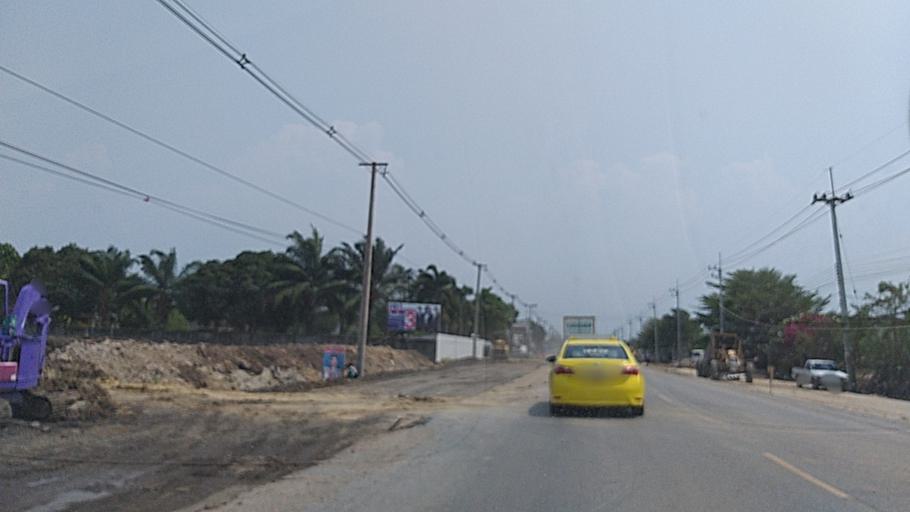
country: TH
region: Chon Buri
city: Phanat Nikhom
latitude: 13.4322
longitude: 101.1818
